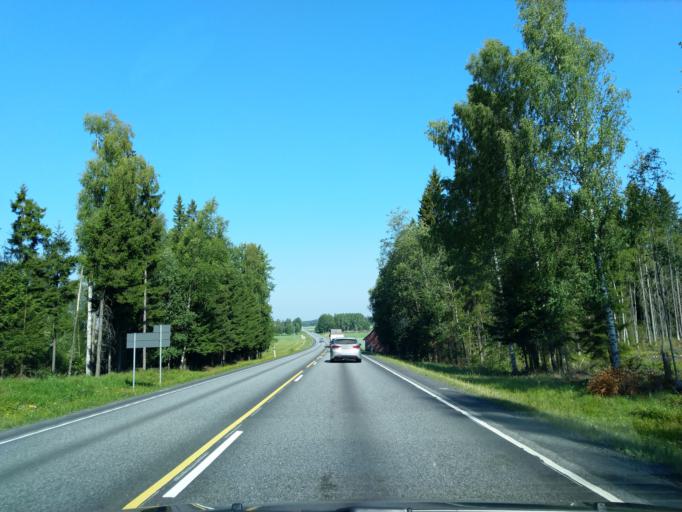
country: FI
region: Varsinais-Suomi
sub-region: Loimaa
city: Alastaro
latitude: 61.0824
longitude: 22.8999
